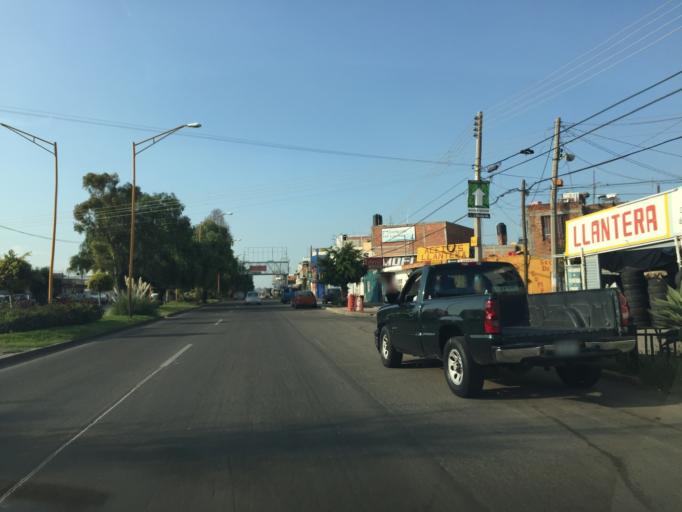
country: MX
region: Aguascalientes
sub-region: Aguascalientes
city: La Loma de los Negritos
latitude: 21.8632
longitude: -102.3172
